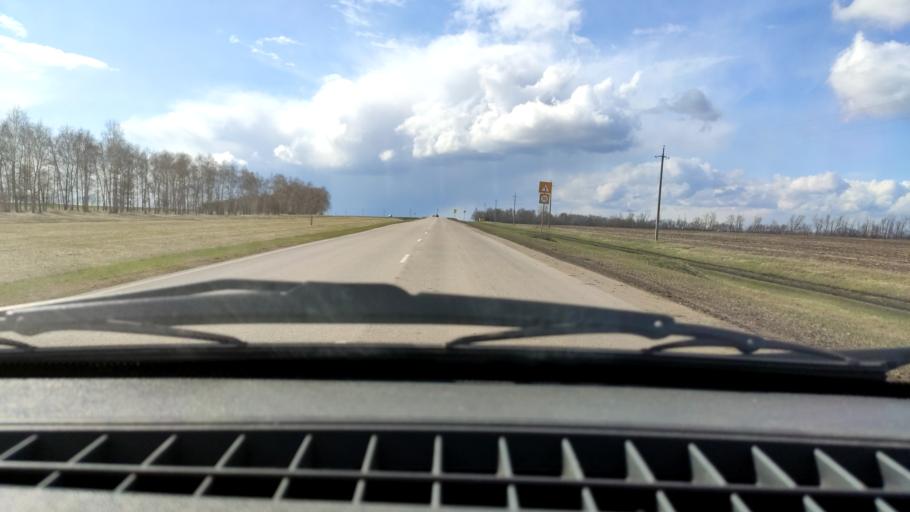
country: RU
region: Bashkortostan
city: Kushnarenkovo
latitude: 55.1017
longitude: 55.0368
